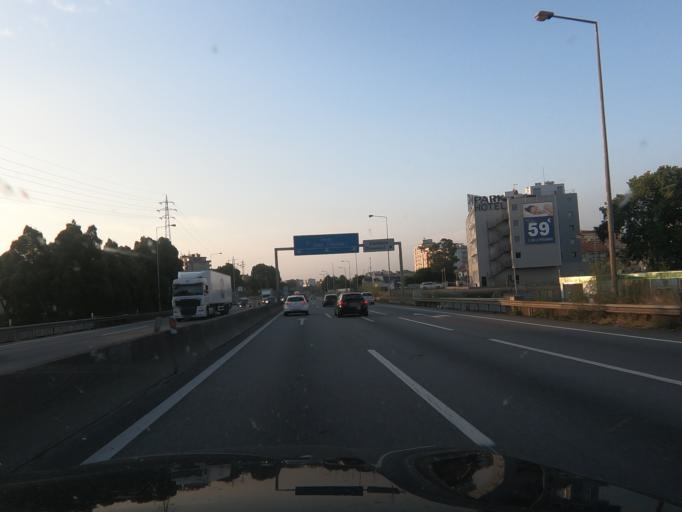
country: PT
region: Porto
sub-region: Vila Nova de Gaia
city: Canidelo
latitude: 41.1256
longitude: -8.6357
